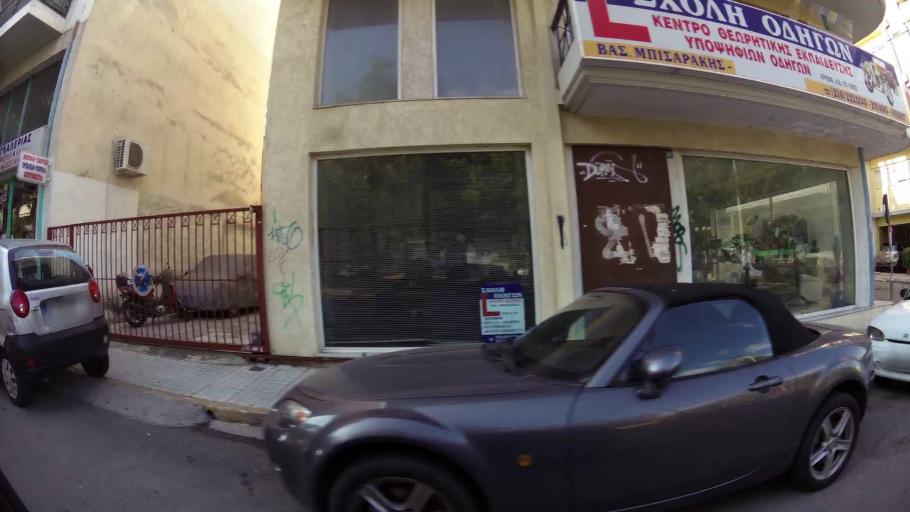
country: GR
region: Attica
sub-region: Nomarchia Athinas
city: Galatsi
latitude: 38.0241
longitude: 23.7463
